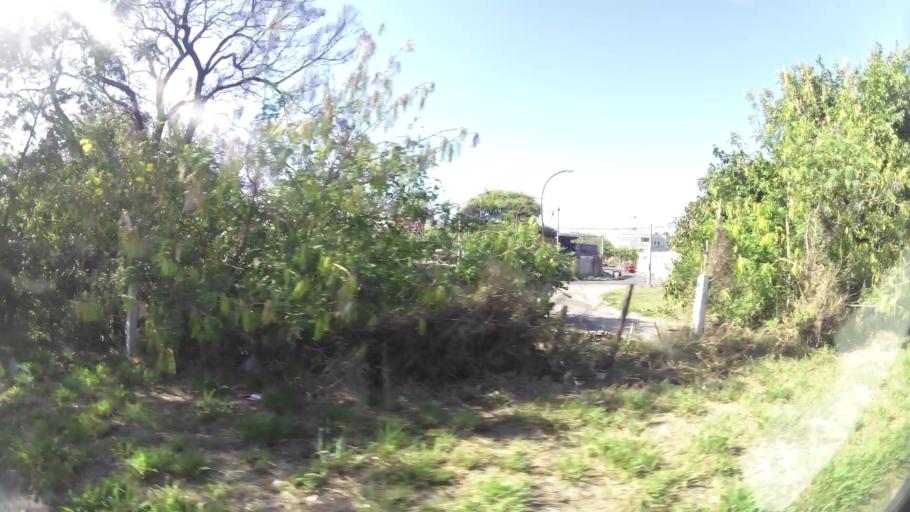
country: AR
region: Cordoba
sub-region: Departamento de Capital
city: Cordoba
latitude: -31.4226
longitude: -64.1629
